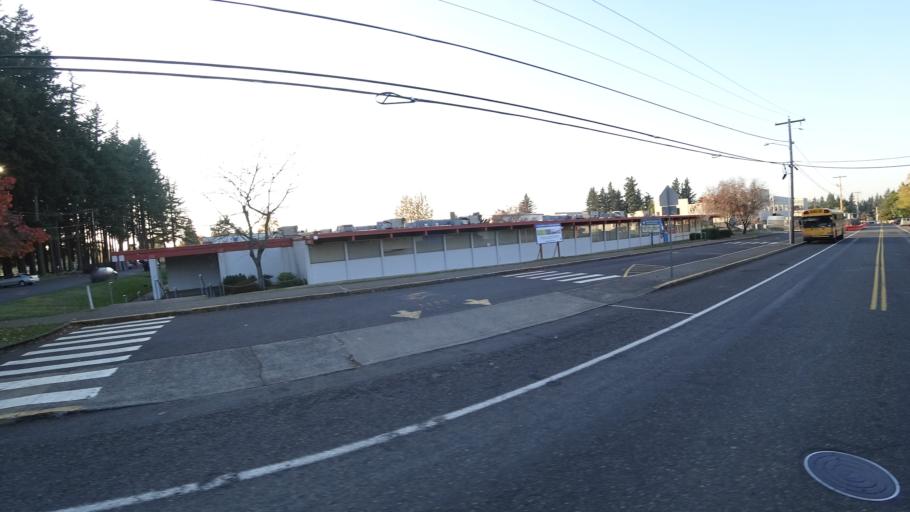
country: US
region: Oregon
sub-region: Multnomah County
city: Gresham
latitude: 45.5152
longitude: -122.4390
